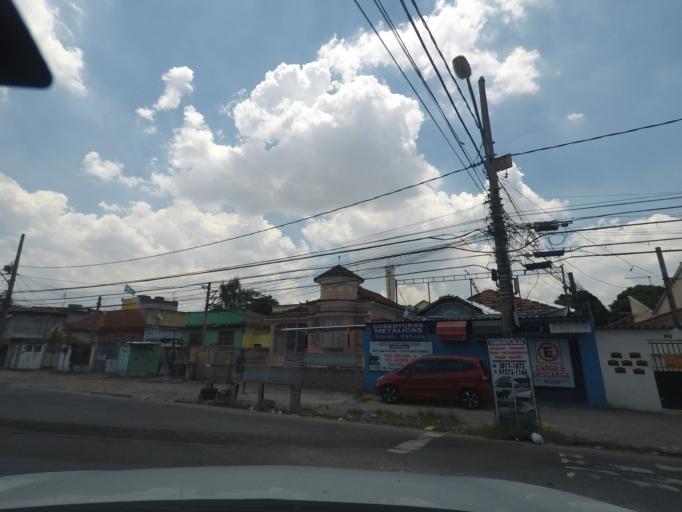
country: BR
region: Rio de Janeiro
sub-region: Sao Joao De Meriti
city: Sao Joao de Meriti
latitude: -22.8619
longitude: -43.3653
